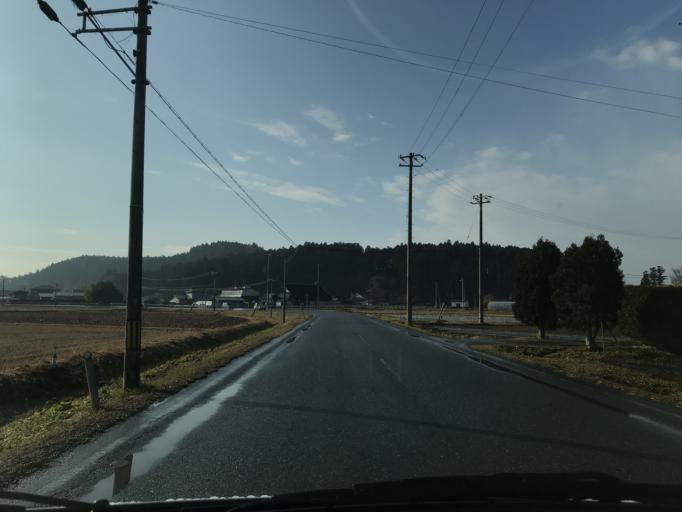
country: JP
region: Iwate
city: Ichinoseki
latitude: 38.7781
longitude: 141.1757
